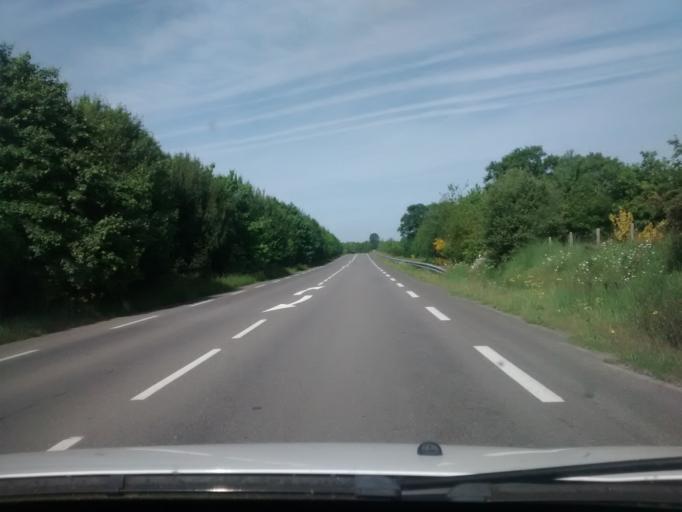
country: FR
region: Brittany
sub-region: Departement d'Ille-et-Vilaine
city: Saint-Brice-en-Cogles
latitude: 48.3948
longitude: -1.3543
